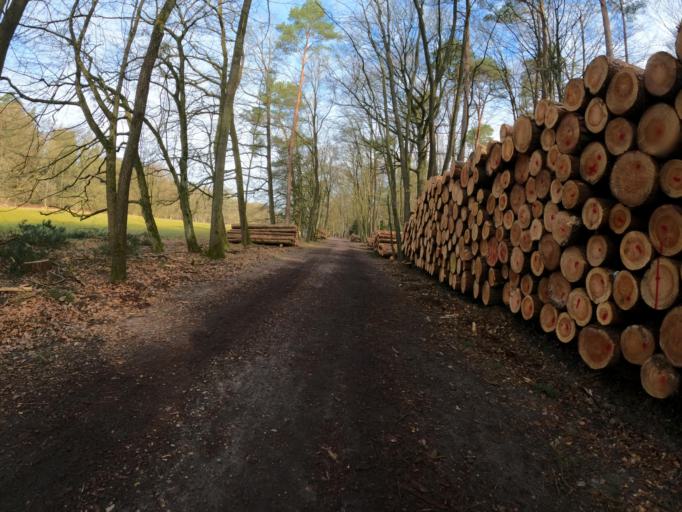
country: DE
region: Lower Saxony
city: Neu Wulmstorf
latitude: 53.4459
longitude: 9.8699
